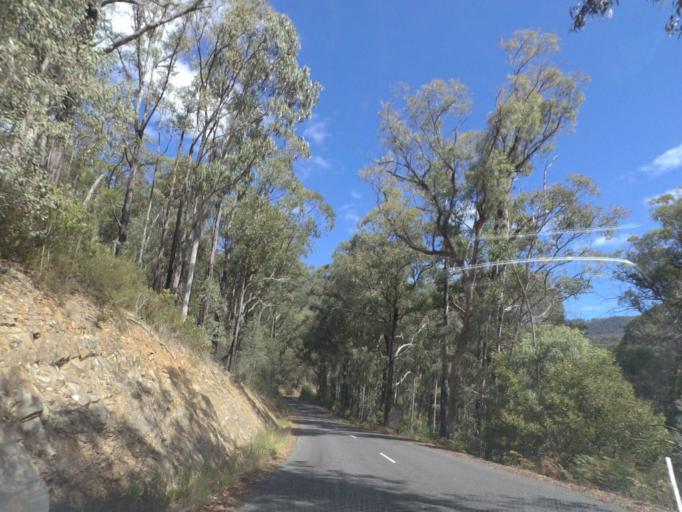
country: AU
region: Victoria
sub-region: Murrindindi
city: Alexandra
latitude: -37.3345
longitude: 145.9536
